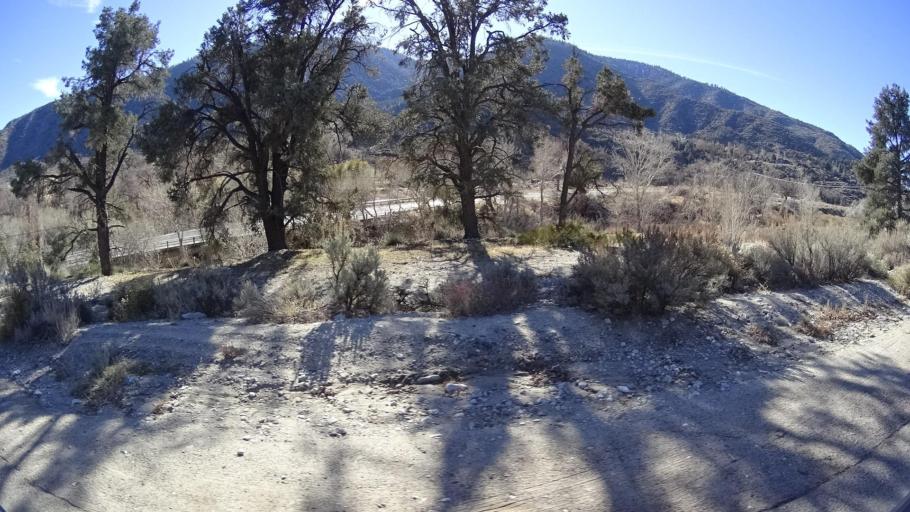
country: US
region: California
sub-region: Kern County
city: Frazier Park
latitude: 34.8199
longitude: -118.9363
